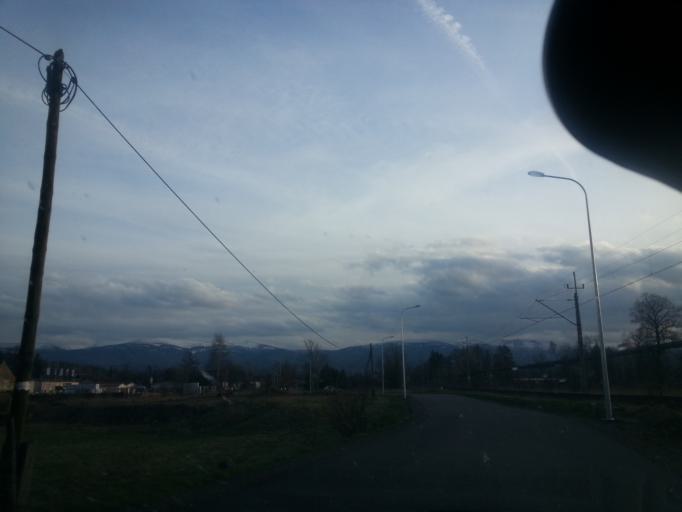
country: PL
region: Lower Silesian Voivodeship
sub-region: Jelenia Gora
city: Cieplice Slaskie Zdroj
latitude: 50.8788
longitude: 15.7000
